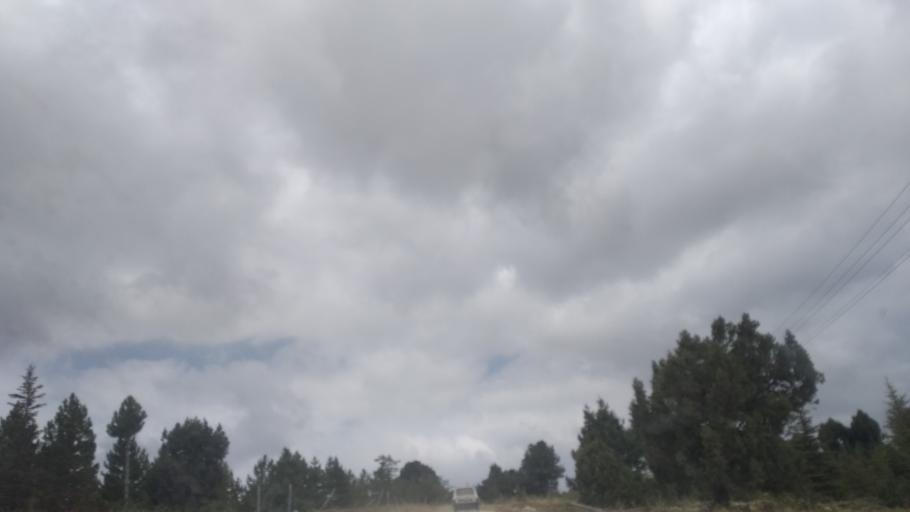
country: TR
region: Mersin
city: Sarikavak
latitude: 36.5698
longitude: 33.7642
